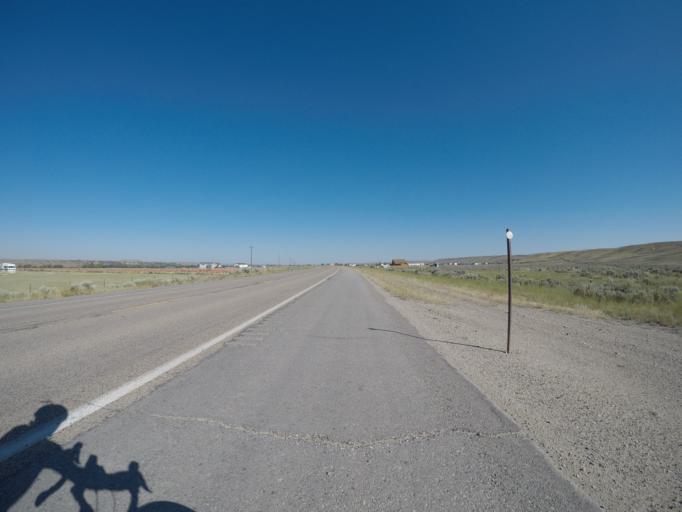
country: US
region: Wyoming
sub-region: Sublette County
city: Pinedale
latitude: 42.7608
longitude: -109.7344
